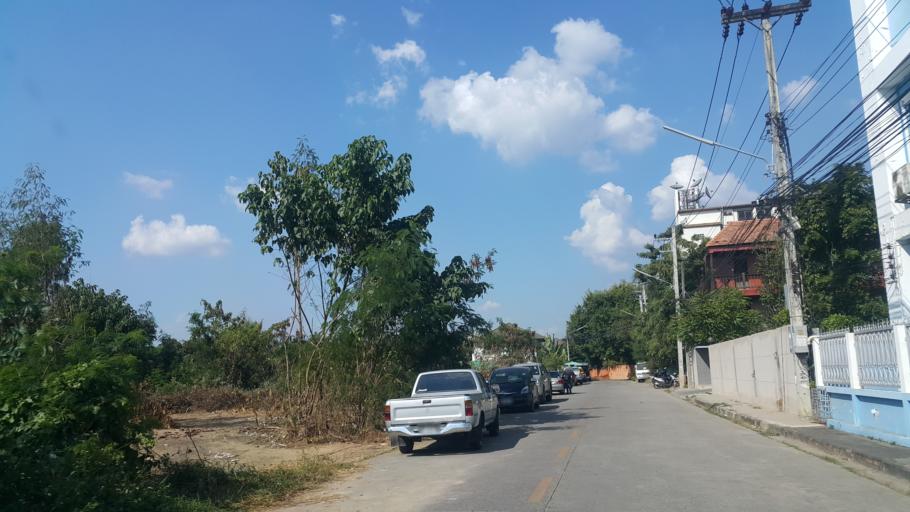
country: TH
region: Chiang Mai
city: Chiang Mai
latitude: 18.7819
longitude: 99.0202
